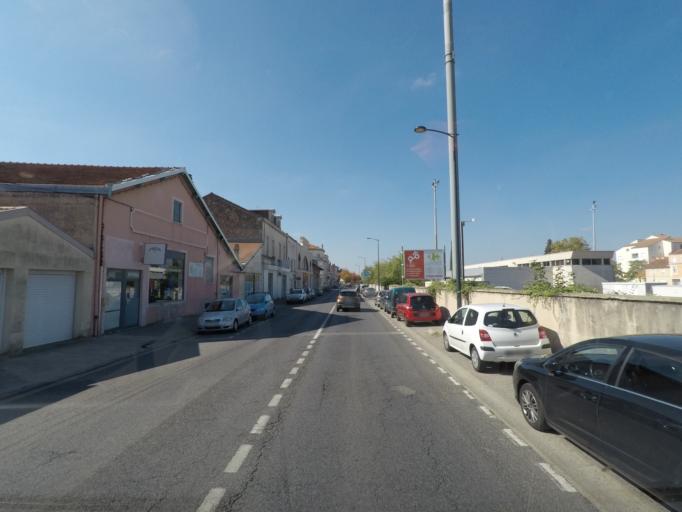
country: FR
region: Rhone-Alpes
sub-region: Departement de la Drome
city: Romans-sur-Isere
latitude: 45.0482
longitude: 5.0533
